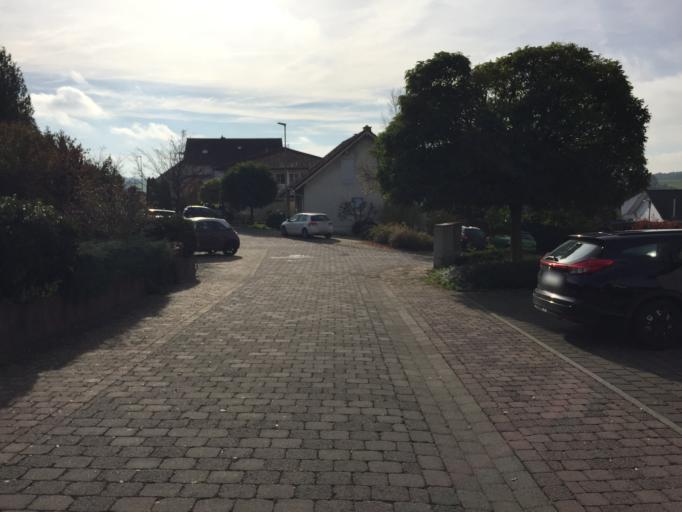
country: DE
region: Hesse
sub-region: Regierungsbezirk Giessen
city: Laubach
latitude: 50.5486
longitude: 8.9820
